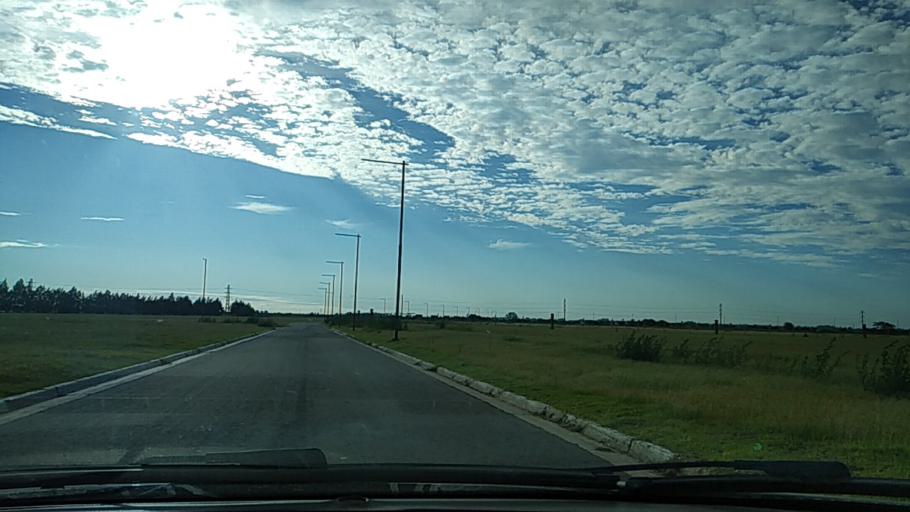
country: AR
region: Santa Fe
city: Funes
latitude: -32.9471
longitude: -60.7729
